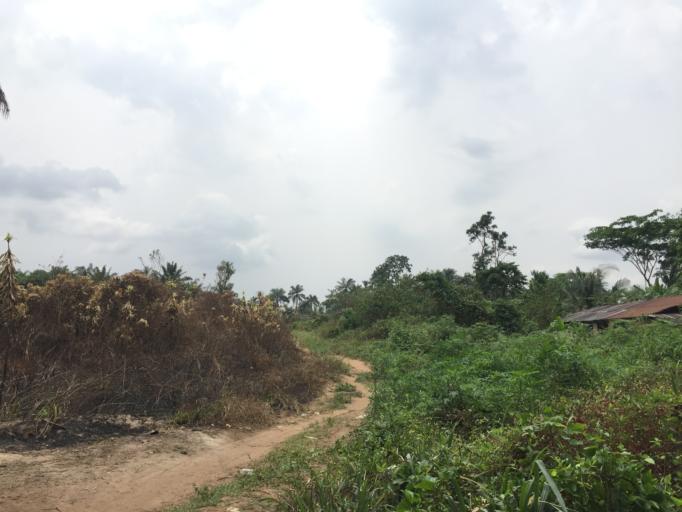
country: NG
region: Imo
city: Ihuo
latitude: 5.4630
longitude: 7.1476
